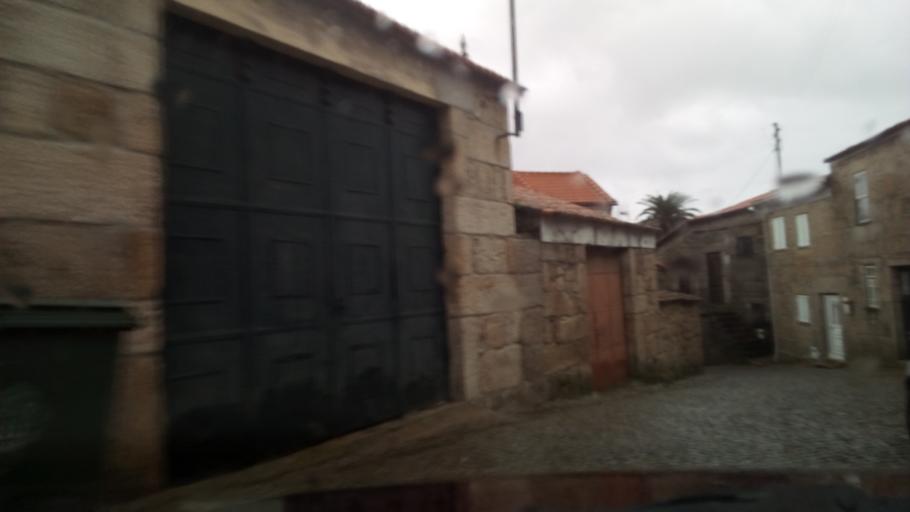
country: PT
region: Guarda
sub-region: Celorico da Beira
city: Celorico da Beira
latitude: 40.6383
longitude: -7.3911
